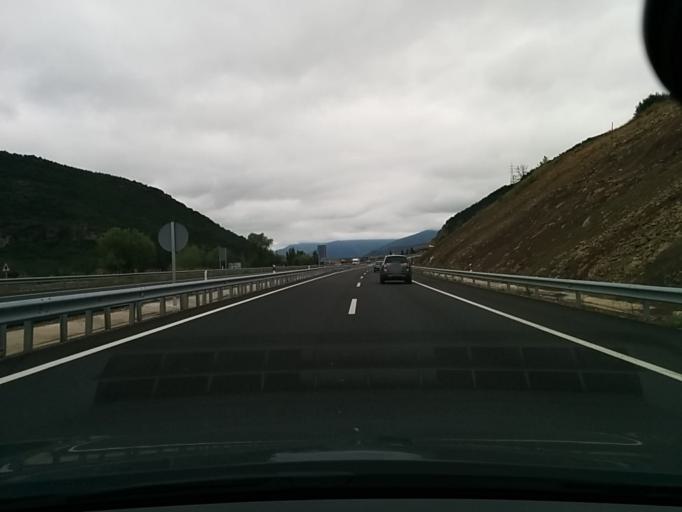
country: ES
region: Aragon
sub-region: Provincia de Huesca
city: Sabinanigo
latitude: 42.4865
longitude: -0.3733
